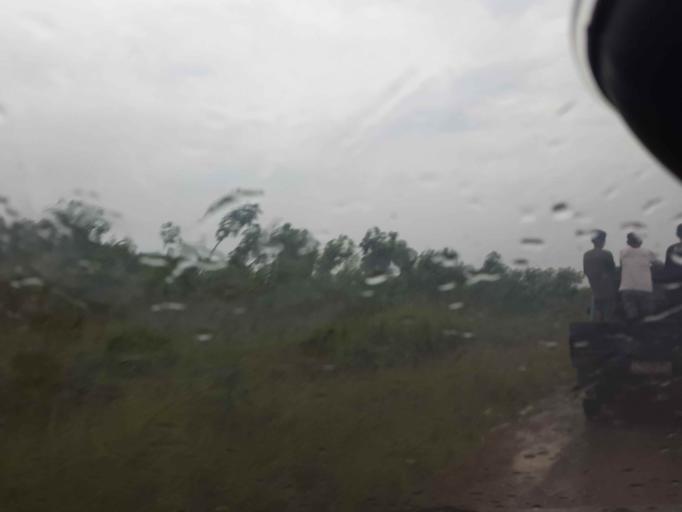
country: ID
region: Lampung
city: Kedaton
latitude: -5.3747
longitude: 105.3217
